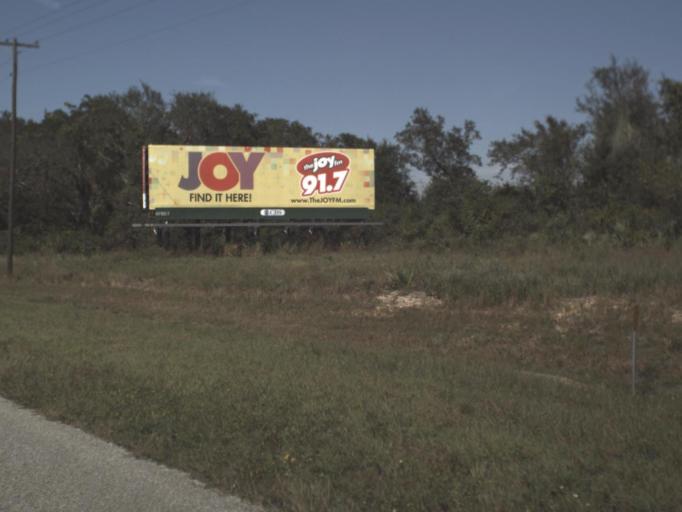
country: US
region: Florida
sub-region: Highlands County
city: Lake Placid
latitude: 27.3854
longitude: -81.4099
